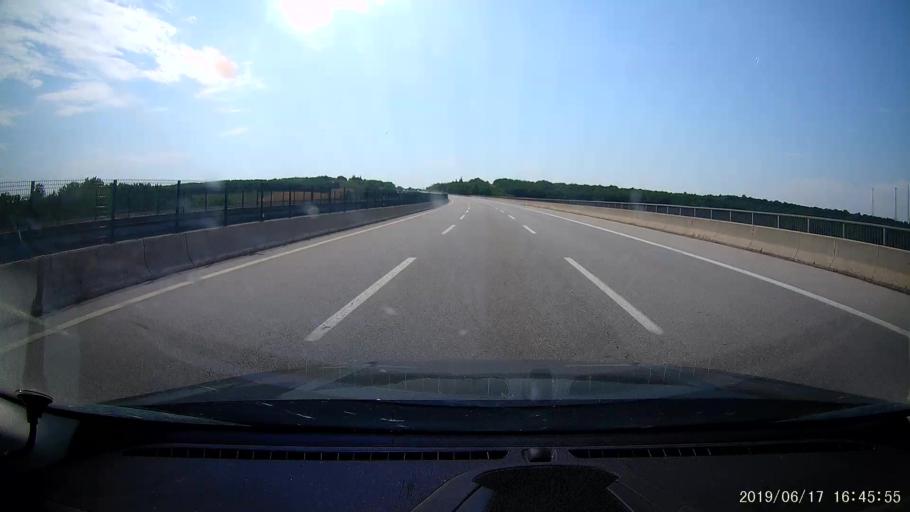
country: TR
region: Kirklareli
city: Babaeski
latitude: 41.4942
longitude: 27.2196
